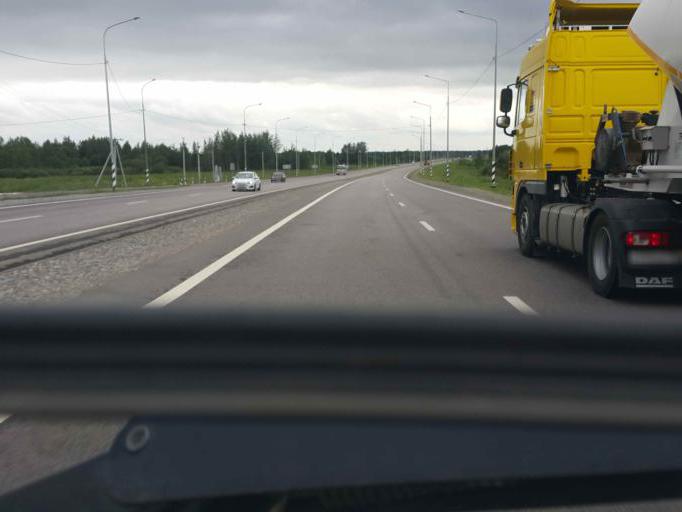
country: RU
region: Tambov
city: Zavoronezhskoye
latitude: 52.8626
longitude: 40.7657
